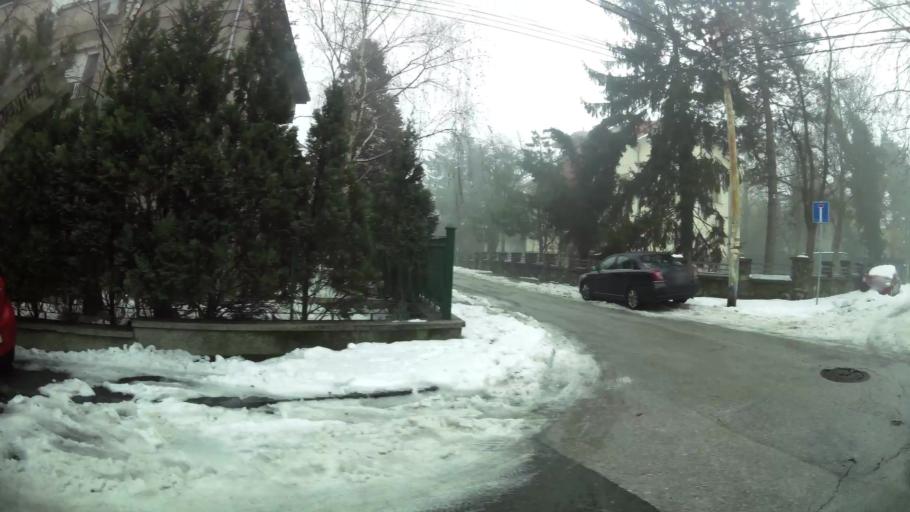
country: RS
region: Central Serbia
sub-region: Belgrade
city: Savski Venac
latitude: 44.7710
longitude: 20.4568
